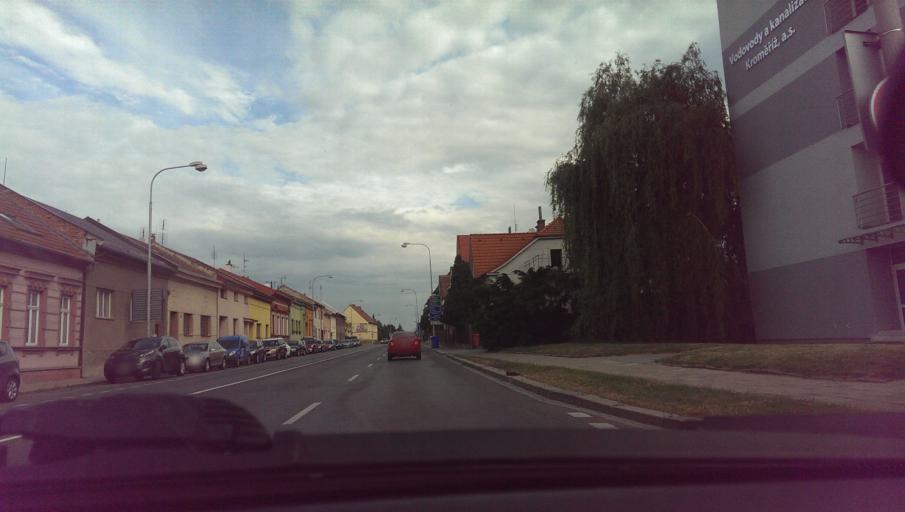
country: CZ
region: Zlin
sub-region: Okres Kromeriz
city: Kromeriz
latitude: 49.3017
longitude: 17.3849
